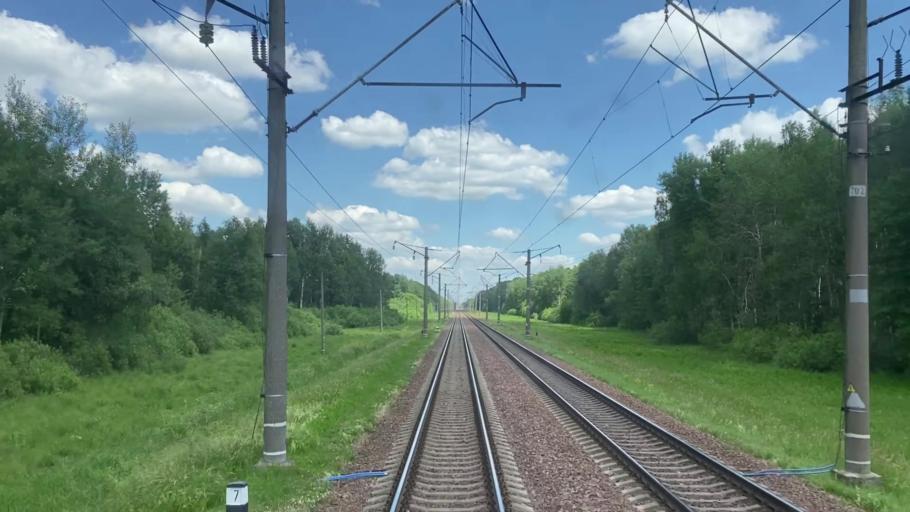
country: BY
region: Brest
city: Pruzhany
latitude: 52.4812
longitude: 24.5574
